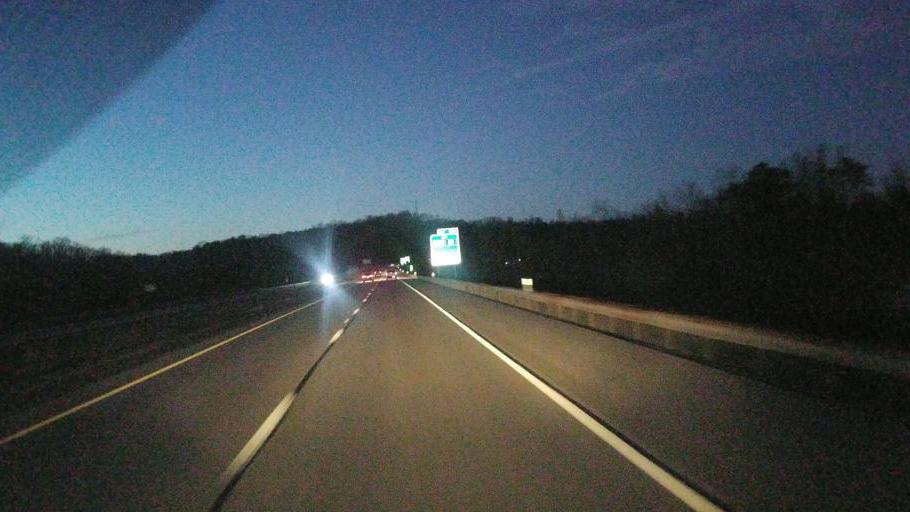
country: US
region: West Virginia
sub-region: Wood County
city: Mineral Wells
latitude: 39.2166
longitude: -81.5246
